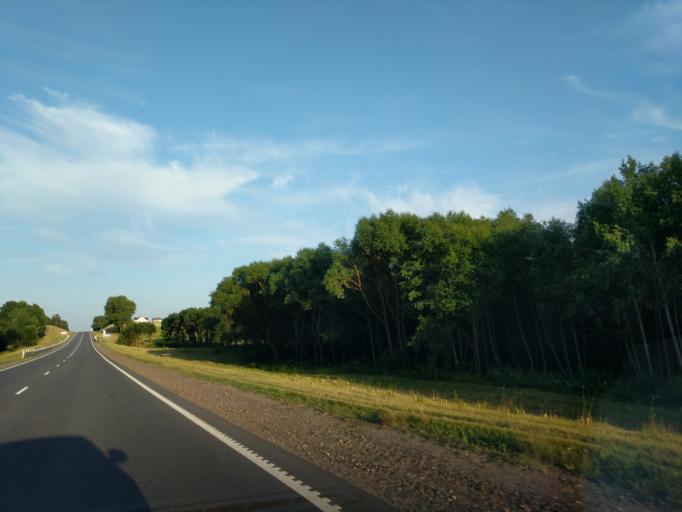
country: BY
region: Minsk
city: Syomkava
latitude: 54.1060
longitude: 27.4673
